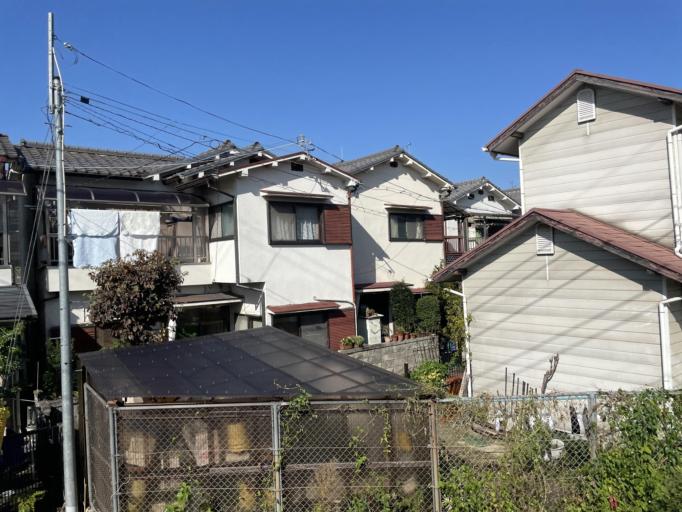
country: JP
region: Nara
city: Nara-shi
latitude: 34.6966
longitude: 135.7777
